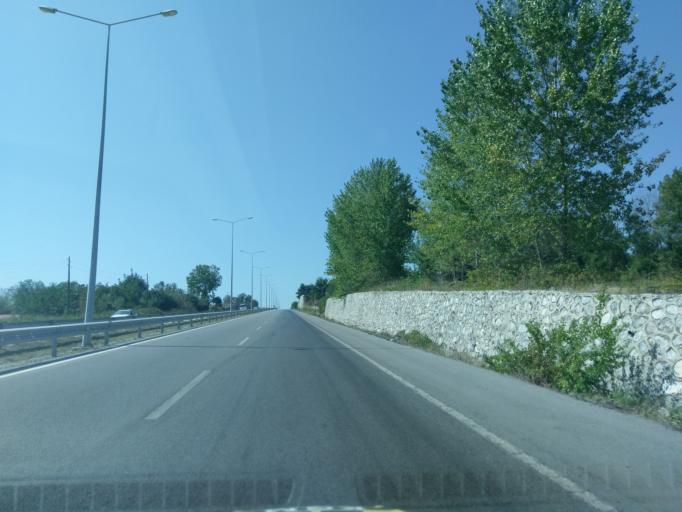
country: TR
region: Samsun
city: Ondokuzmayis
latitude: 41.5225
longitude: 35.9845
